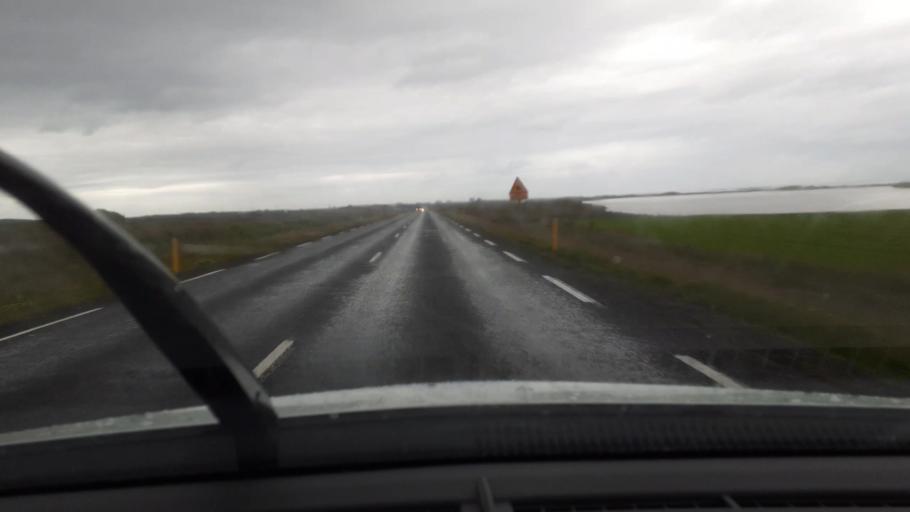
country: IS
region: West
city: Akranes
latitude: 64.3498
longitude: -21.9991
